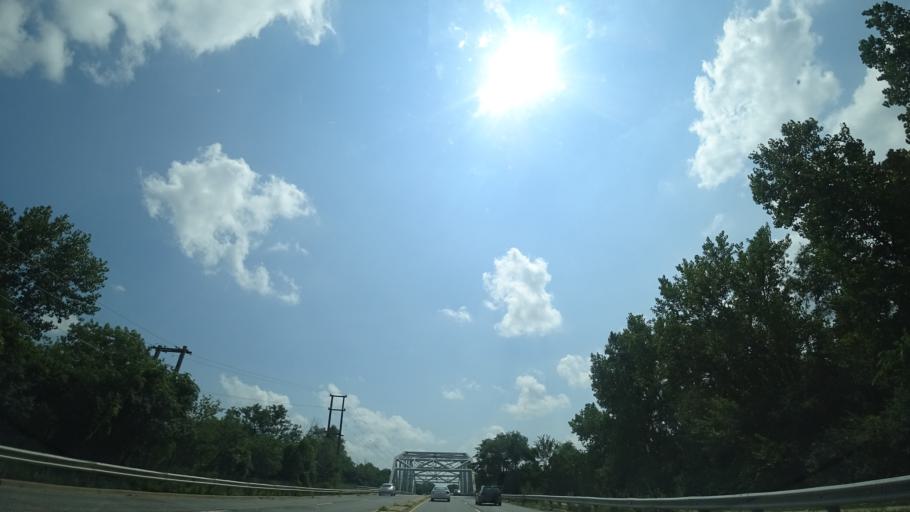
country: US
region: Illinois
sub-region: Cook County
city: Palos Heights
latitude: 41.6789
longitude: -87.7970
